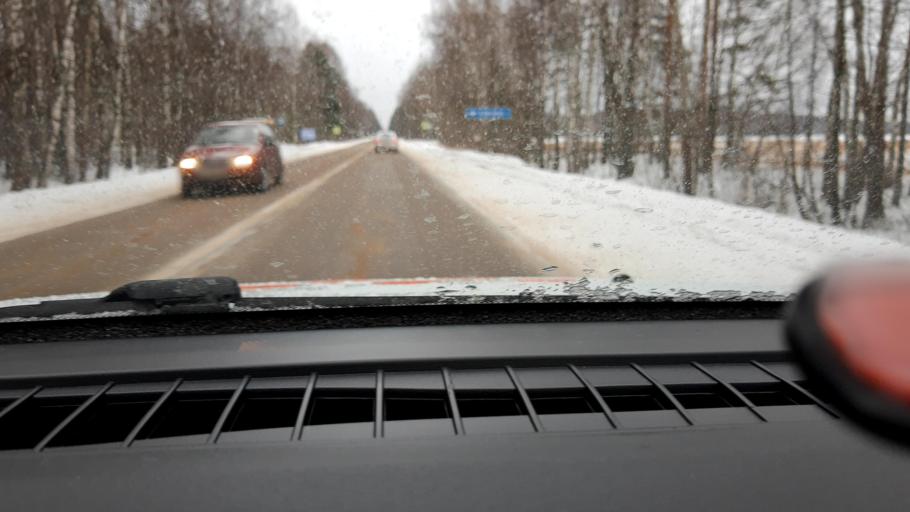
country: RU
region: Nizjnij Novgorod
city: Kstovo
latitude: 56.2957
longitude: 44.2756
